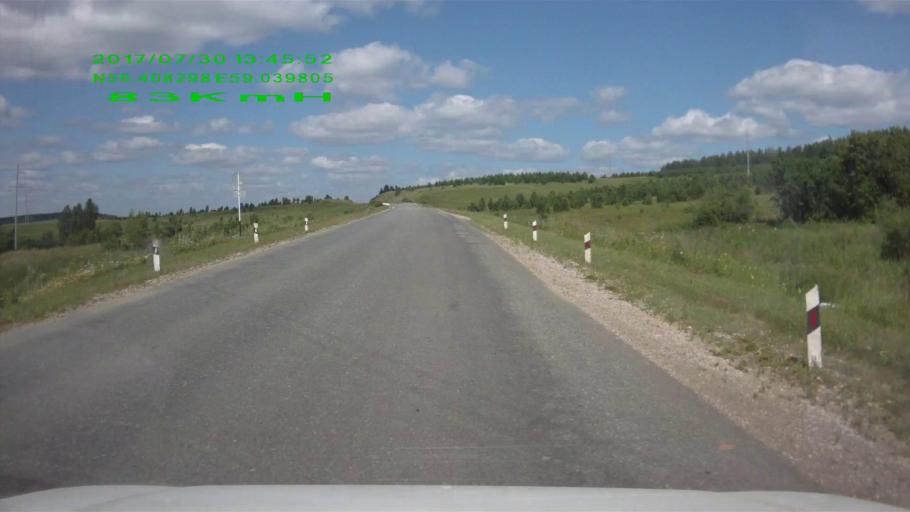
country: RU
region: Sverdlovsk
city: Mikhaylovsk
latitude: 56.4087
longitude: 59.0399
